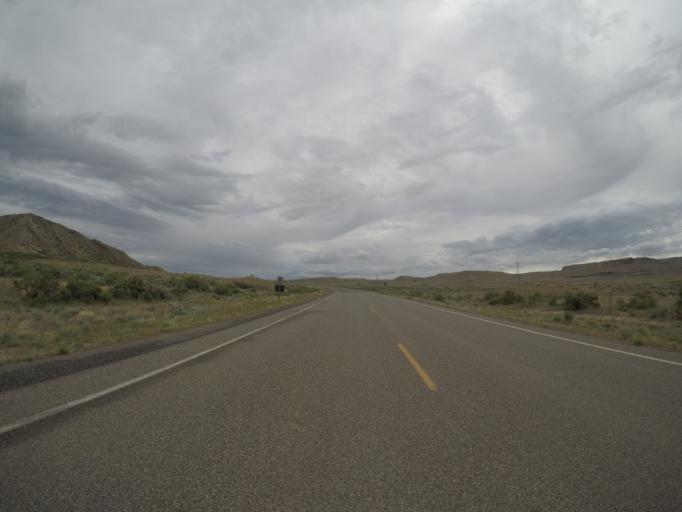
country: US
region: Wyoming
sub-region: Big Horn County
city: Lovell
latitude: 44.9508
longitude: -108.2962
